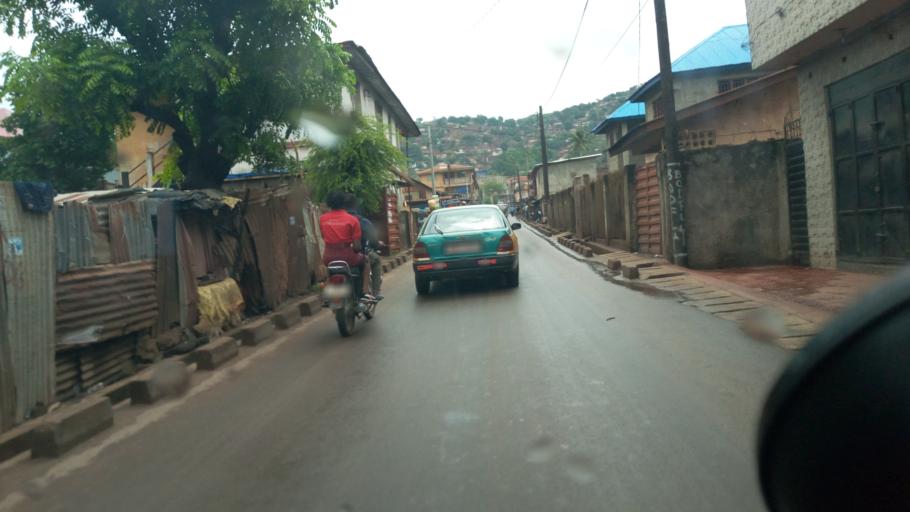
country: SL
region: Western Area
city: Freetown
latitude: 8.4771
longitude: -13.2353
